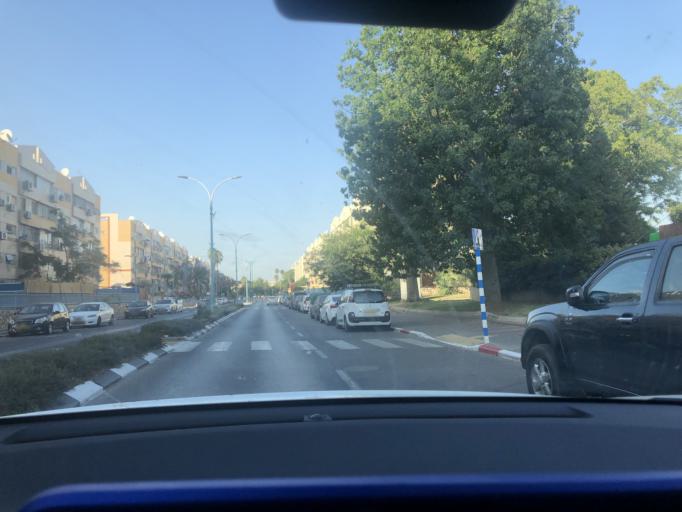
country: IL
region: Central District
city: Lod
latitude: 31.9492
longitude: 34.8828
